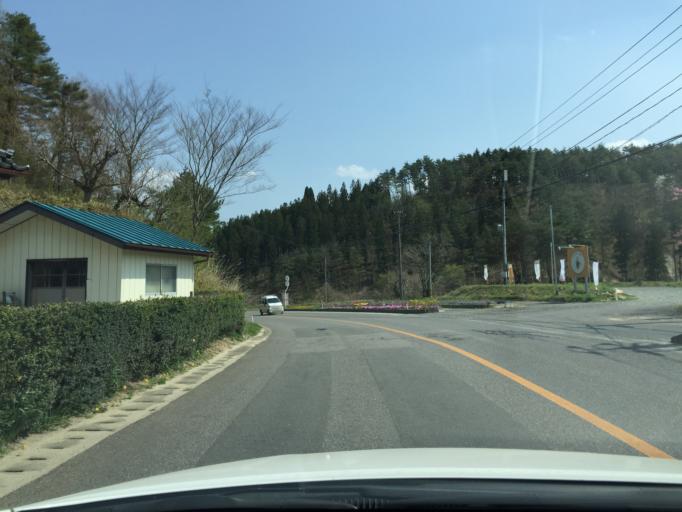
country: JP
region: Fukushima
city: Funehikimachi-funehiki
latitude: 37.4520
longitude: 140.7665
